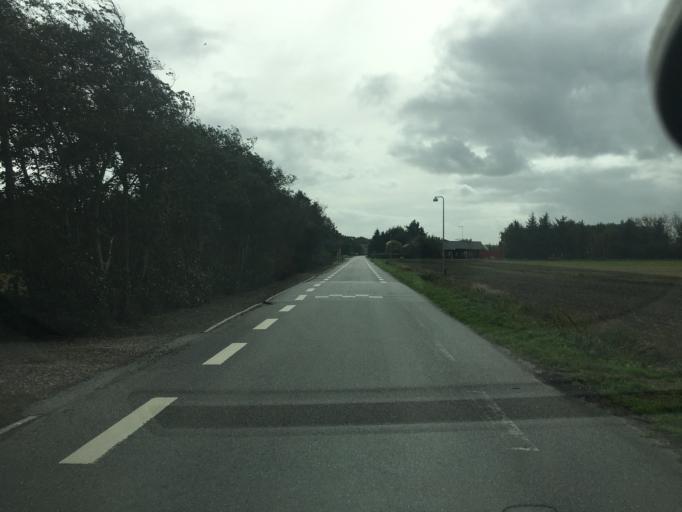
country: DE
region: Schleswig-Holstein
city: Aventoft
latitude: 54.9710
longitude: 8.7687
